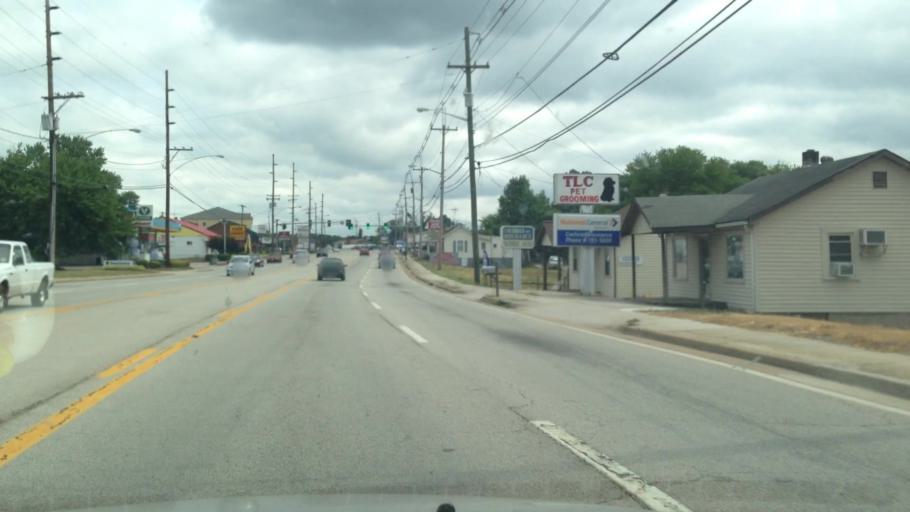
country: US
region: Virginia
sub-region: City of Danville
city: Danville
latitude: 36.6075
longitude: -79.4094
